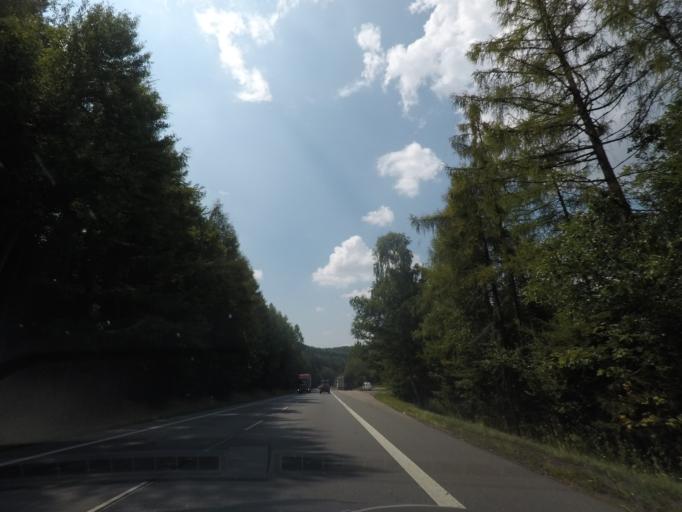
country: CZ
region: Pardubicky
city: Mestecko Trnavka
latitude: 49.7628
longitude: 16.7952
